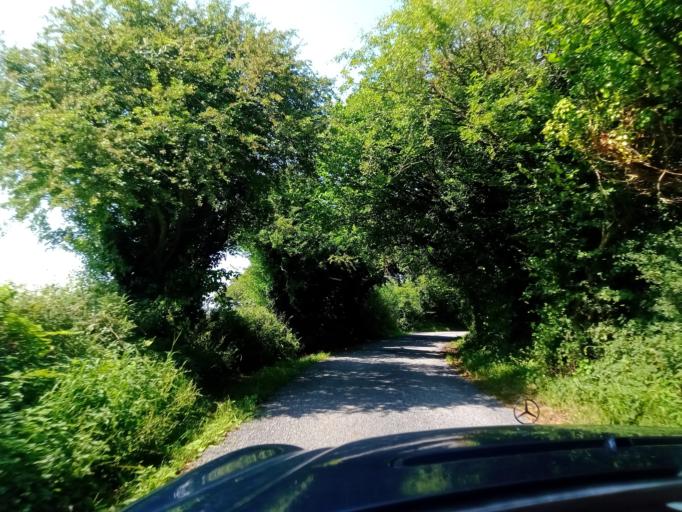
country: IE
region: Leinster
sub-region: Kilkenny
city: Mooncoin
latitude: 52.3177
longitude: -7.2827
